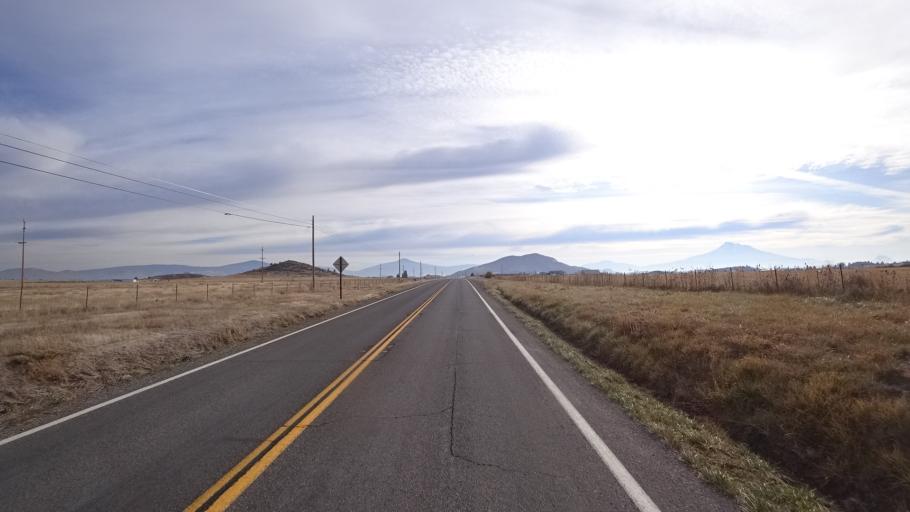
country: US
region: California
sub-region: Siskiyou County
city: Montague
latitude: 41.7252
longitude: -122.5527
